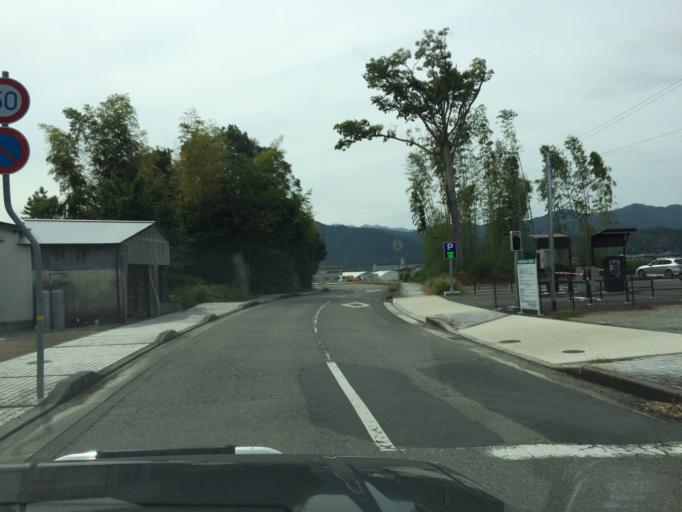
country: JP
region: Hyogo
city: Sasayama
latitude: 35.0748
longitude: 135.2137
